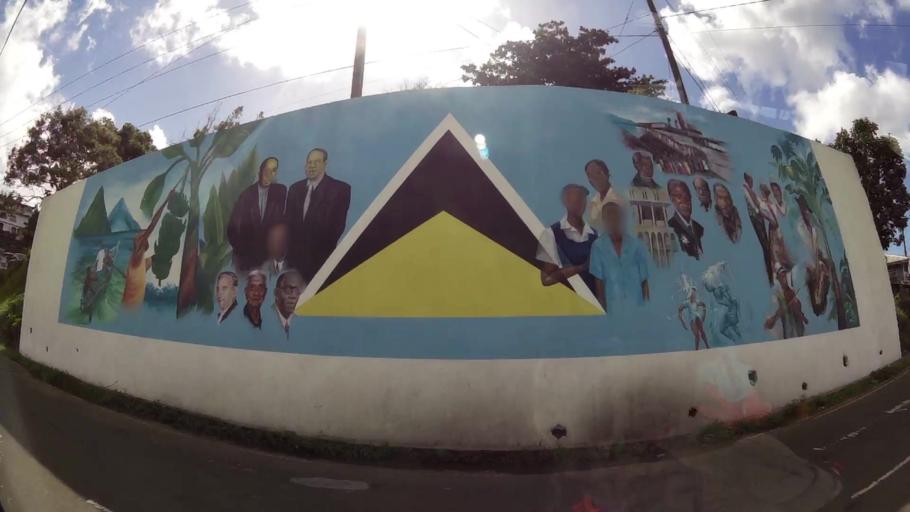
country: LC
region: Castries Quarter
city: Castries
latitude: 14.0089
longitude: -60.9938
